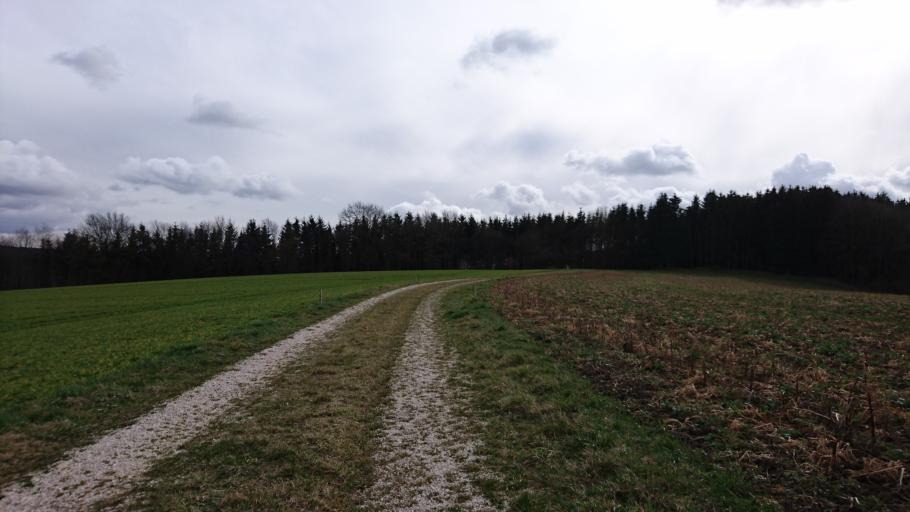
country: DE
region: Bavaria
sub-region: Swabia
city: Altenmunster
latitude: 48.4359
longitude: 10.5881
